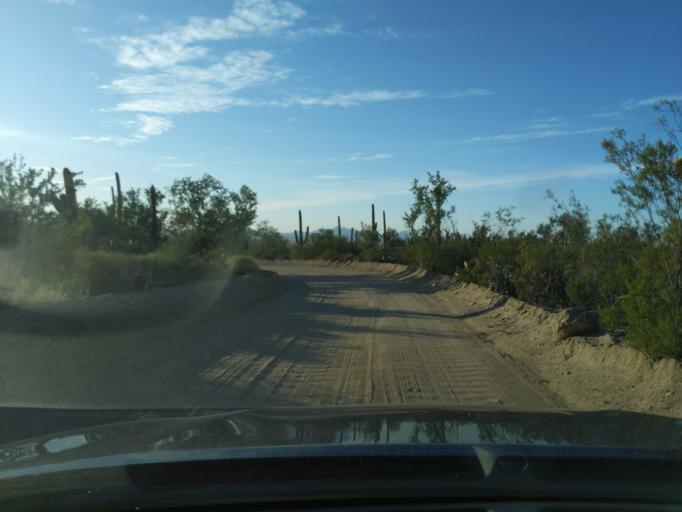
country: US
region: Arizona
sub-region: Pima County
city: Picture Rocks
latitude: 32.2882
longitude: -111.1901
